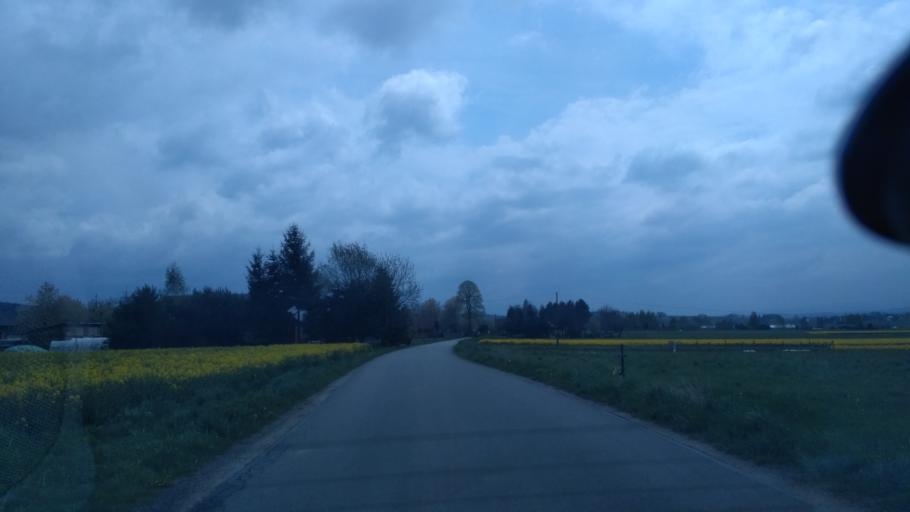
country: PL
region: Subcarpathian Voivodeship
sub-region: Powiat brzozowski
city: Jablonica Polska
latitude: 49.6813
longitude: 21.8989
